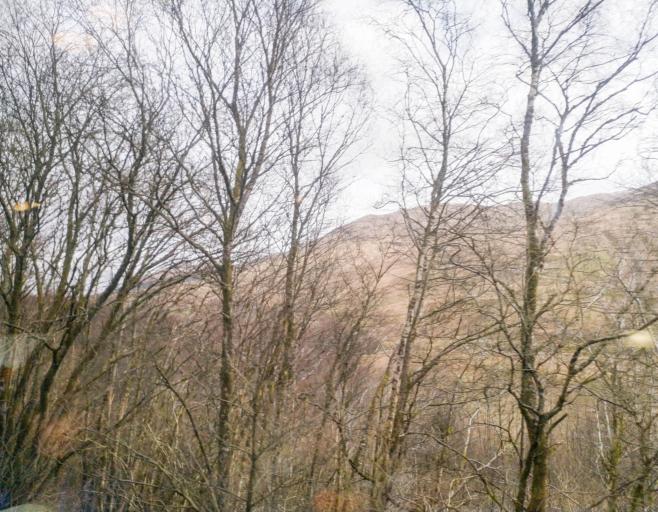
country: GB
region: Scotland
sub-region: Argyll and Bute
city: Garelochhead
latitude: 56.3588
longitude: -4.6792
